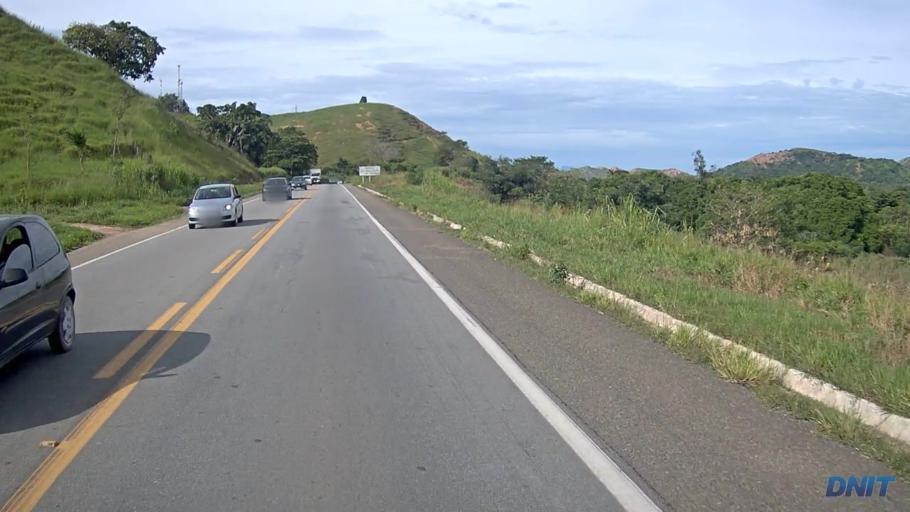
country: BR
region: Minas Gerais
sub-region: Belo Oriente
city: Belo Oriente
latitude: -19.1683
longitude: -42.2467
